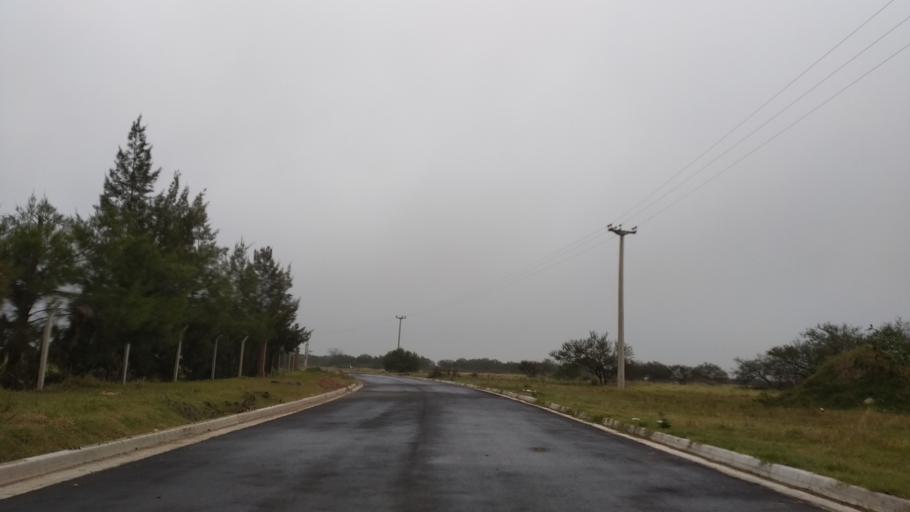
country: AR
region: Santa Fe
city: Funes
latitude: -32.9361
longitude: -60.7657
